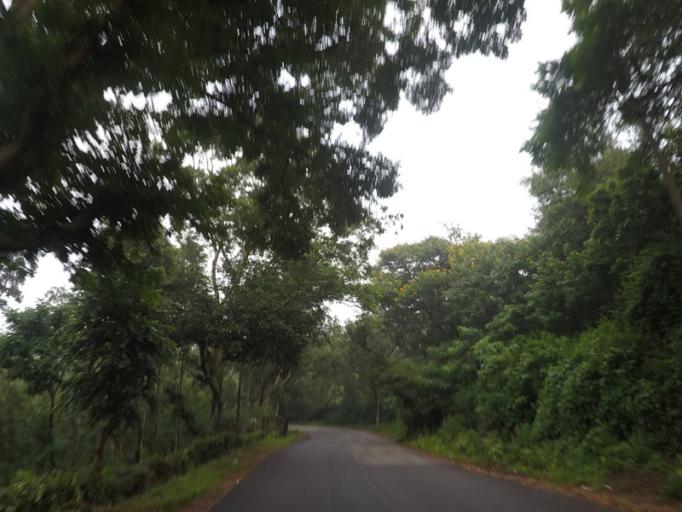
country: IN
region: Karnataka
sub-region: Chikmagalur
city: Chikmagalur
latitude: 13.3679
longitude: 75.7503
